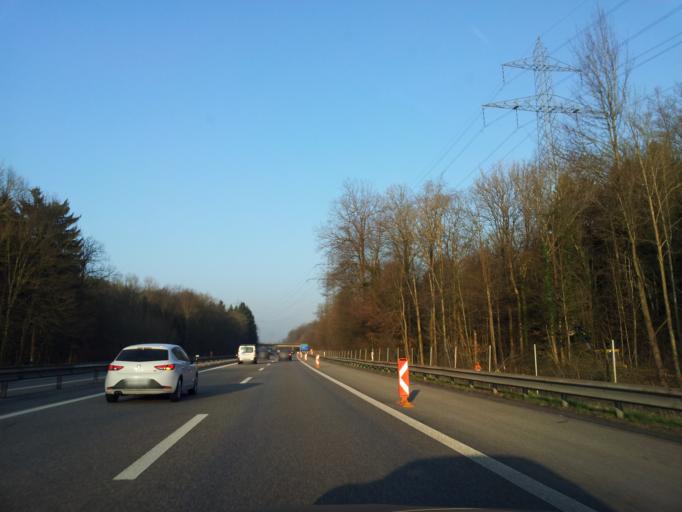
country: CH
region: Aargau
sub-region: Bezirk Rheinfelden
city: Magden
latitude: 47.5459
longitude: 7.8166
